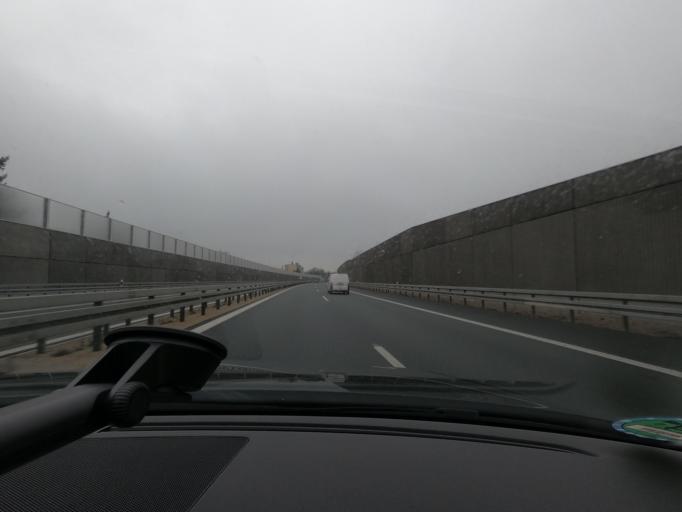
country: DE
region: Bavaria
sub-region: Upper Franconia
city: Forchheim
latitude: 49.7304
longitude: 11.0542
